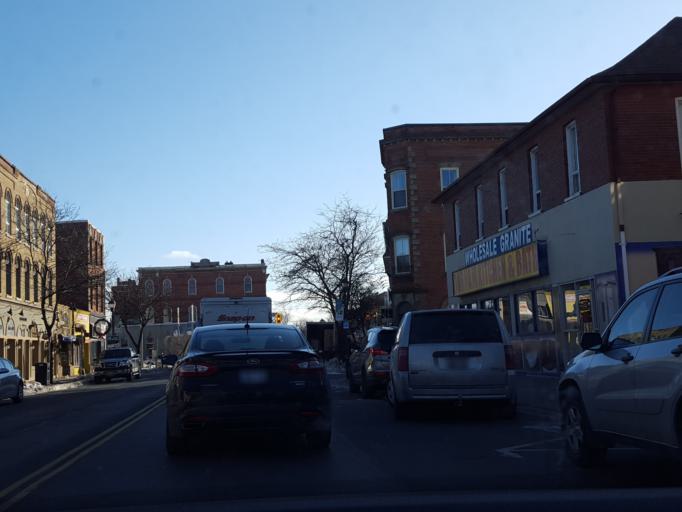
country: CA
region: Ontario
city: Oshawa
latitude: 43.8809
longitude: -78.9425
